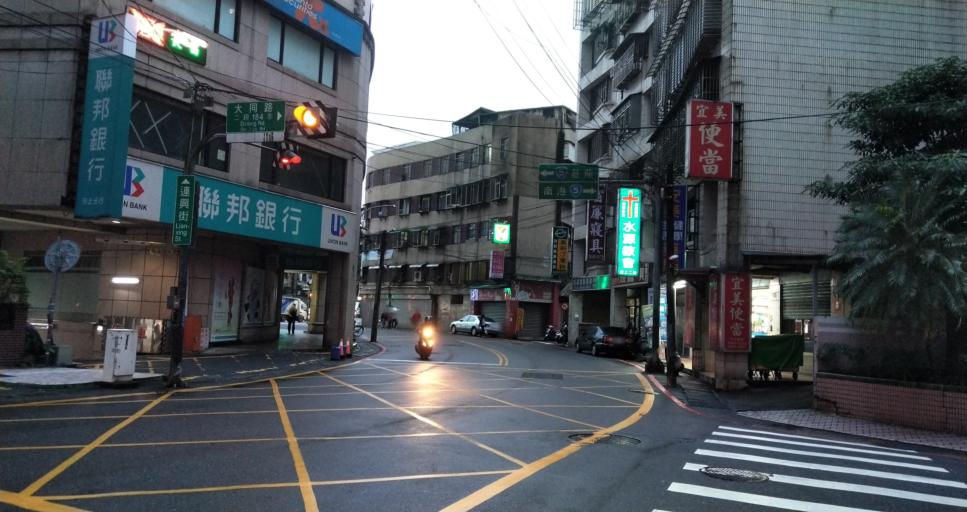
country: TW
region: Taiwan
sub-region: Keelung
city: Keelung
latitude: 25.0630
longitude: 121.6538
